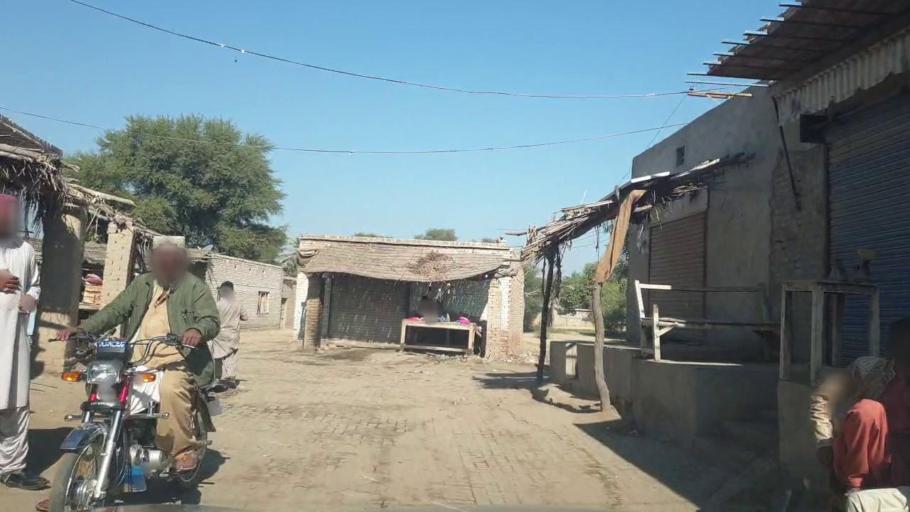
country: PK
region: Sindh
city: Mirpur Mathelo
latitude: 28.1431
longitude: 69.5338
